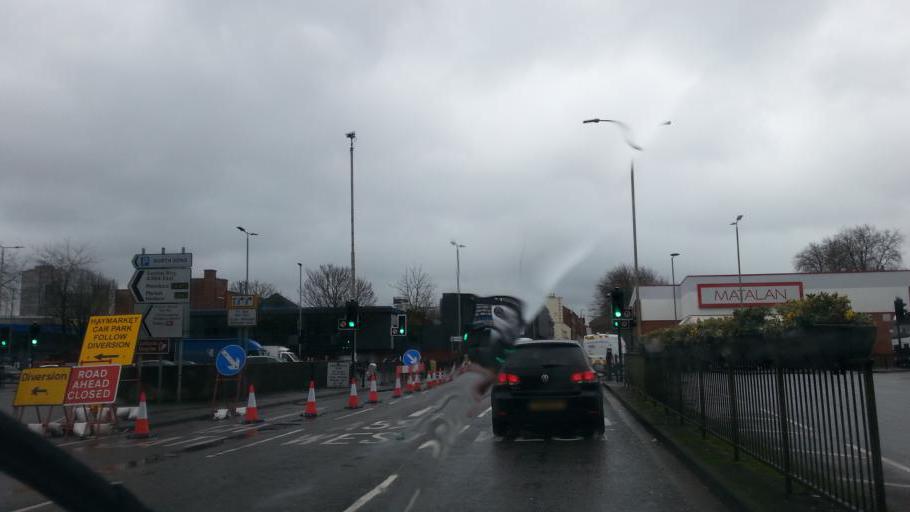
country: GB
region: England
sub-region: City of Leicester
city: Leicester
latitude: 52.6398
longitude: -1.1364
